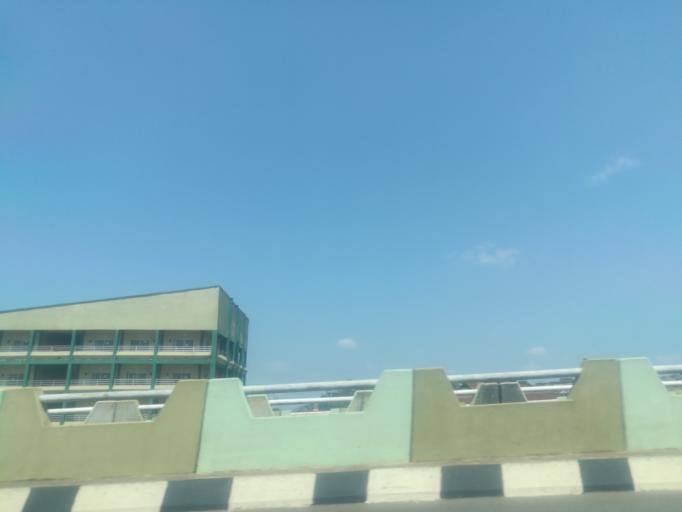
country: NG
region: Ogun
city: Abeokuta
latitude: 7.1568
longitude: 3.3413
